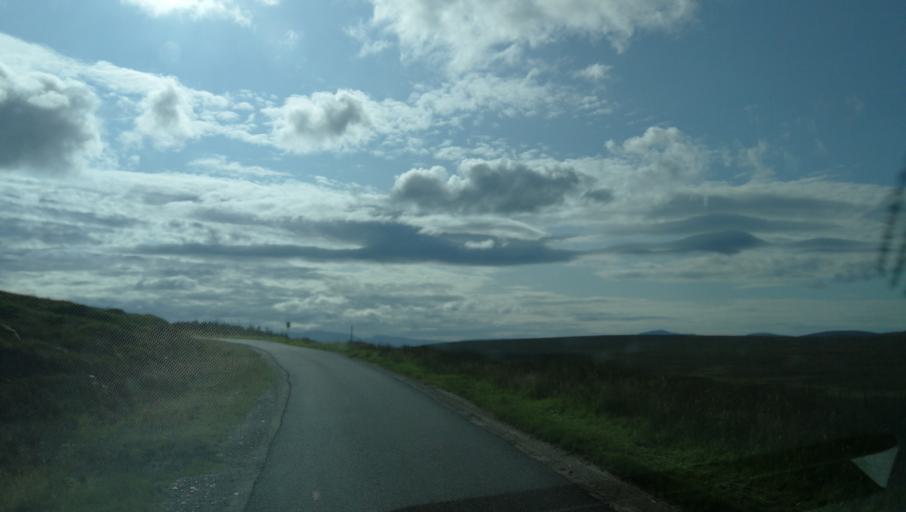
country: GB
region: Scotland
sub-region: Highland
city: Evanton
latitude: 58.2026
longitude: -4.5101
